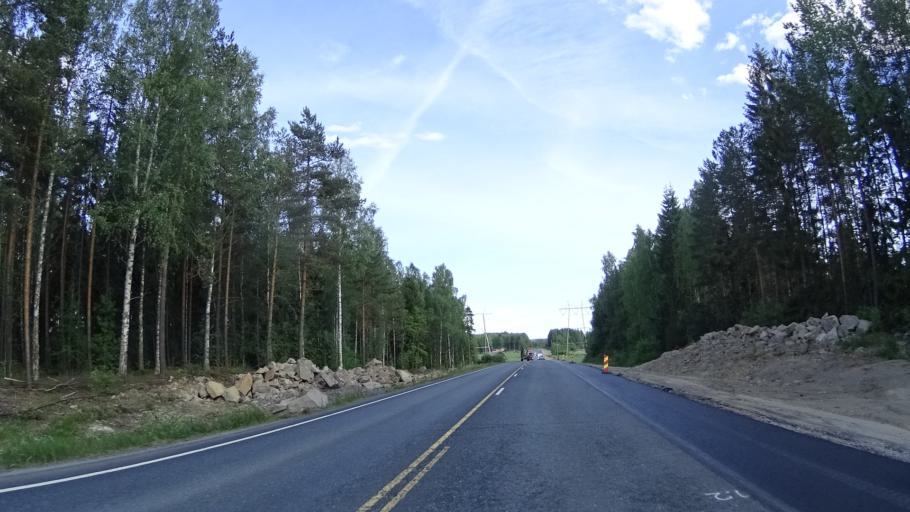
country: FI
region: Haeme
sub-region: Forssa
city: Forssa
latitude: 60.7775
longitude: 23.6705
